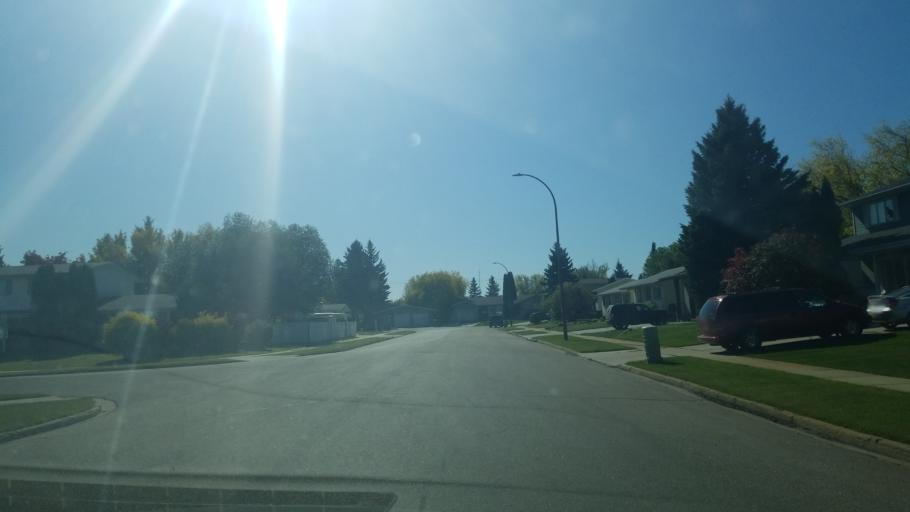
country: CA
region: Saskatchewan
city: Lloydminster
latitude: 53.2723
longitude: -110.0203
